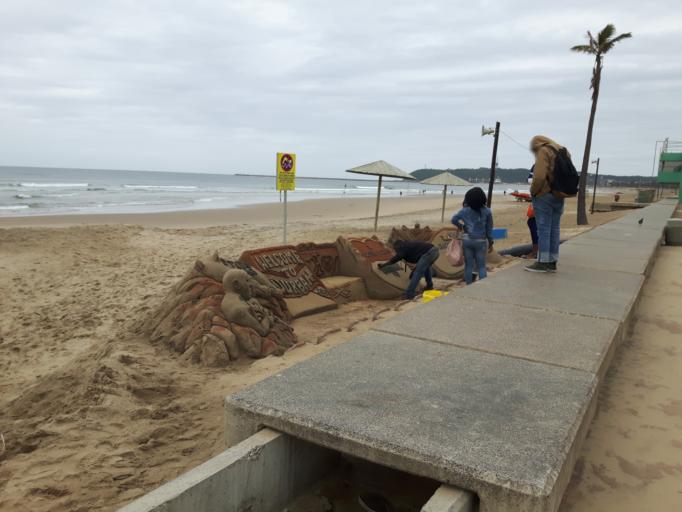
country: ZA
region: KwaZulu-Natal
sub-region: eThekwini Metropolitan Municipality
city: Durban
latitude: -29.8531
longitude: 31.0397
